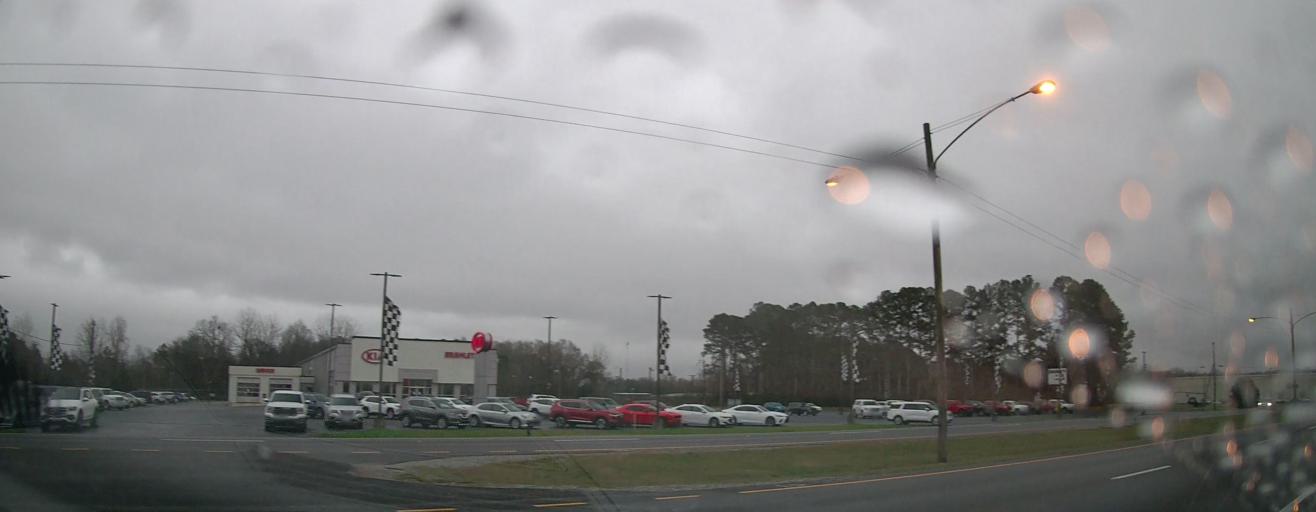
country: US
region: Alabama
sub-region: Morgan County
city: Flint City
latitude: 34.5465
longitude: -86.9738
